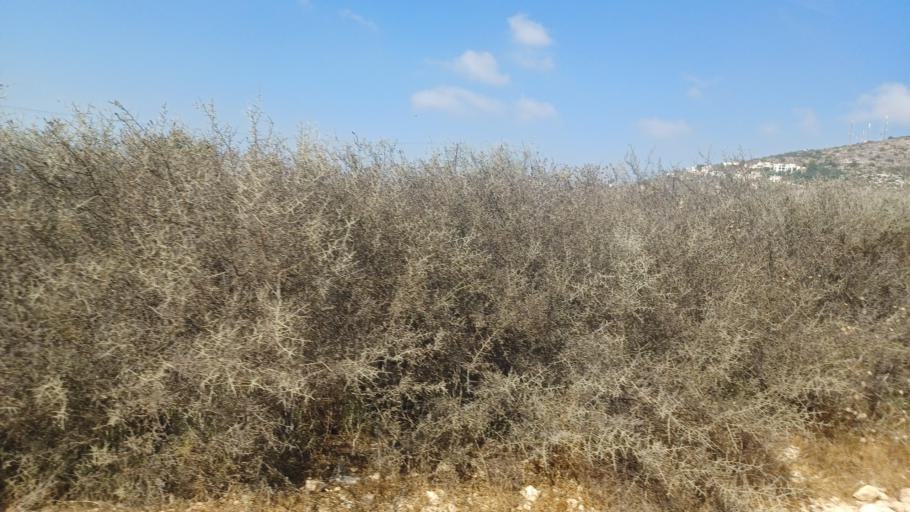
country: CY
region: Pafos
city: Mesogi
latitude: 34.8310
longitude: 32.4567
